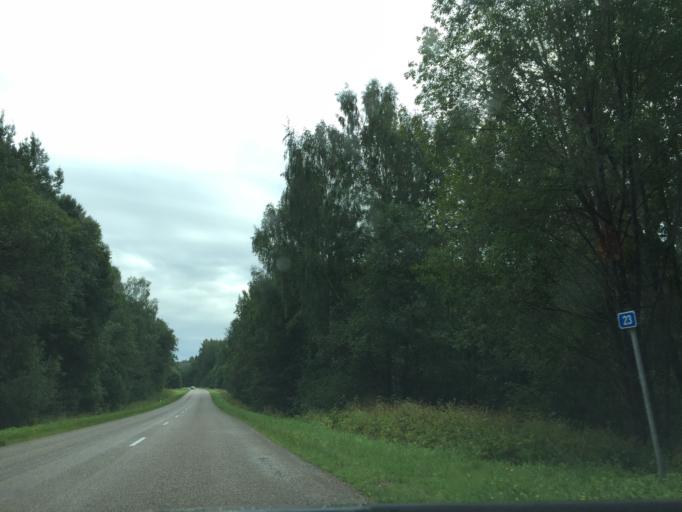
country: LV
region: Dagda
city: Dagda
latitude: 56.1934
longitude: 27.3362
